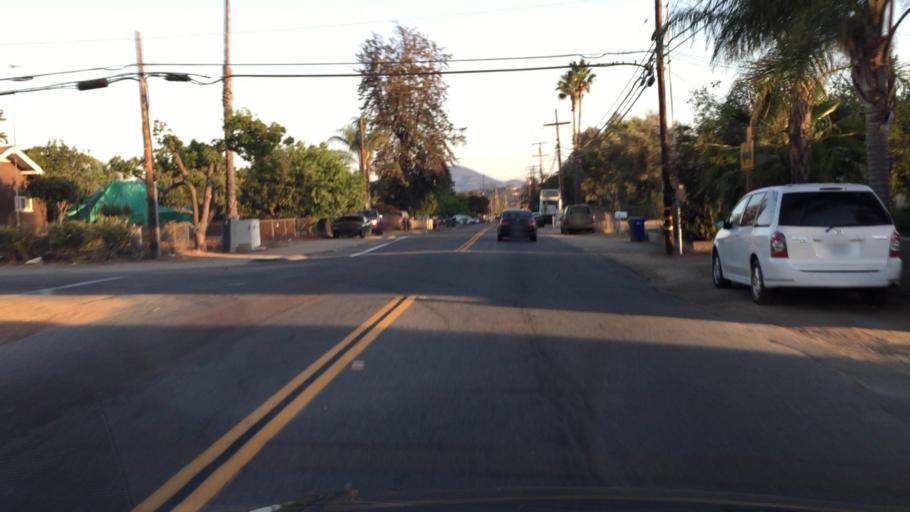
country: US
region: California
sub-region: San Diego County
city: Bostonia
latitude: 32.8117
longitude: -116.9446
